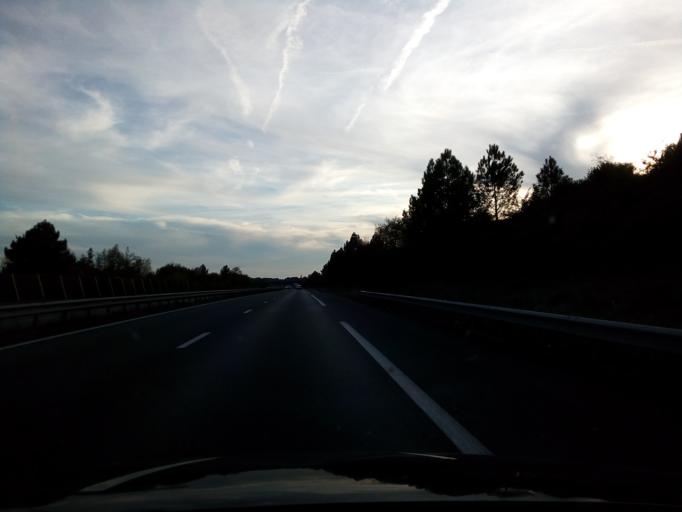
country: FR
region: Poitou-Charentes
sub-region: Departement de la Charente-Maritime
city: Montlieu-la-Garde
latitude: 45.2082
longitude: -0.2981
